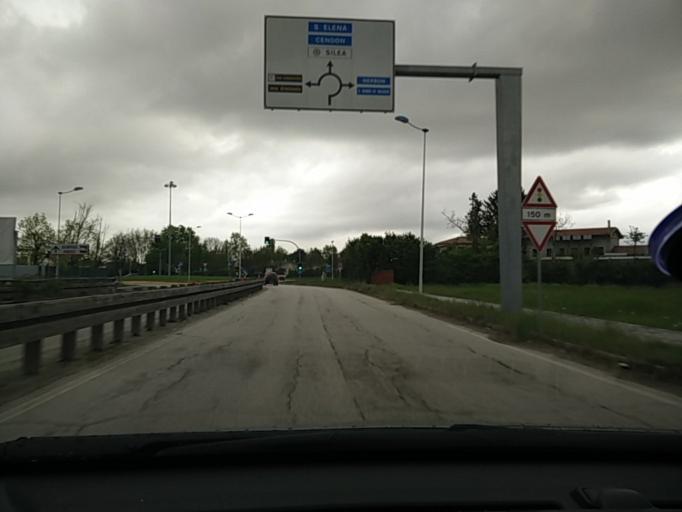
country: IT
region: Veneto
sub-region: Provincia di Treviso
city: Silea
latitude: 45.6513
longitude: 12.3098
